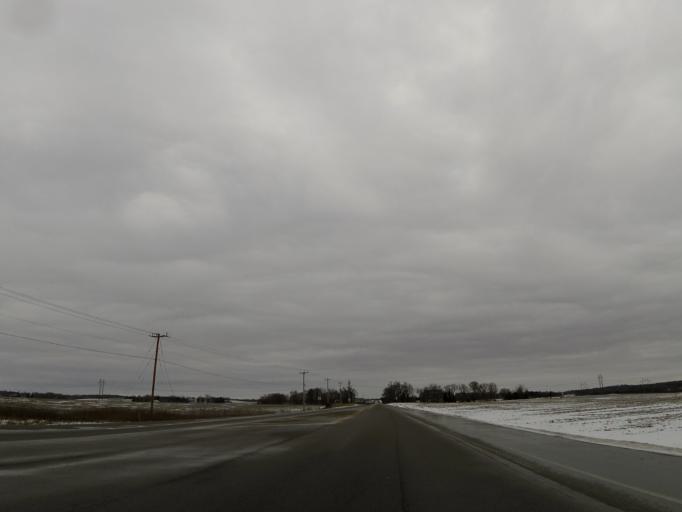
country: US
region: Minnesota
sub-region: Washington County
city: Woodbury
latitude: 44.8874
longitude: -92.9033
